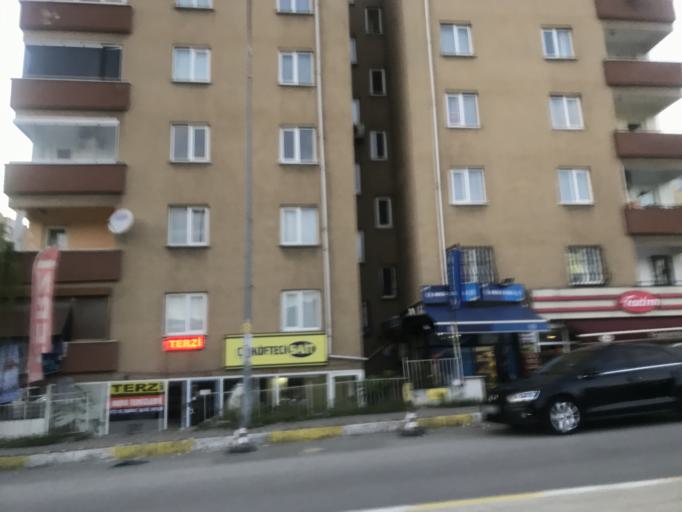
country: TR
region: Istanbul
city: Umraniye
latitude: 41.0341
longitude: 29.0983
